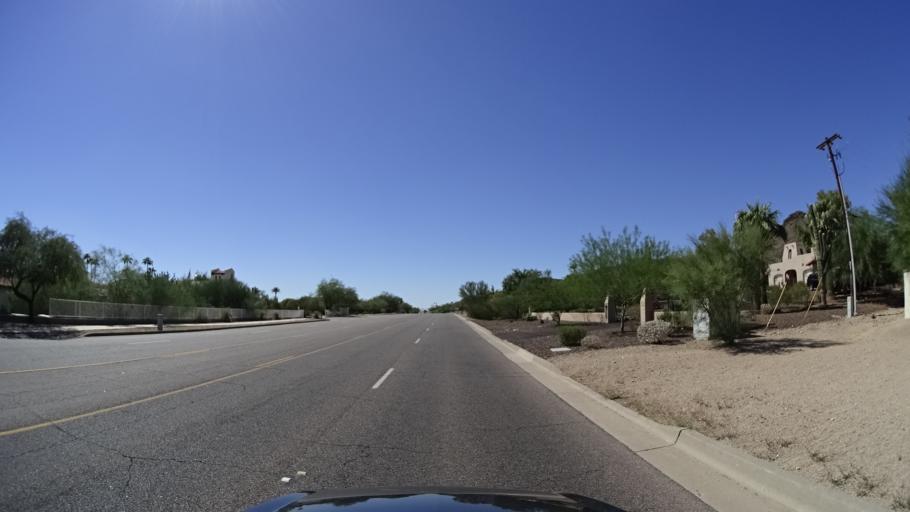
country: US
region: Arizona
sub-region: Maricopa County
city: Paradise Valley
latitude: 33.5318
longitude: -111.9936
